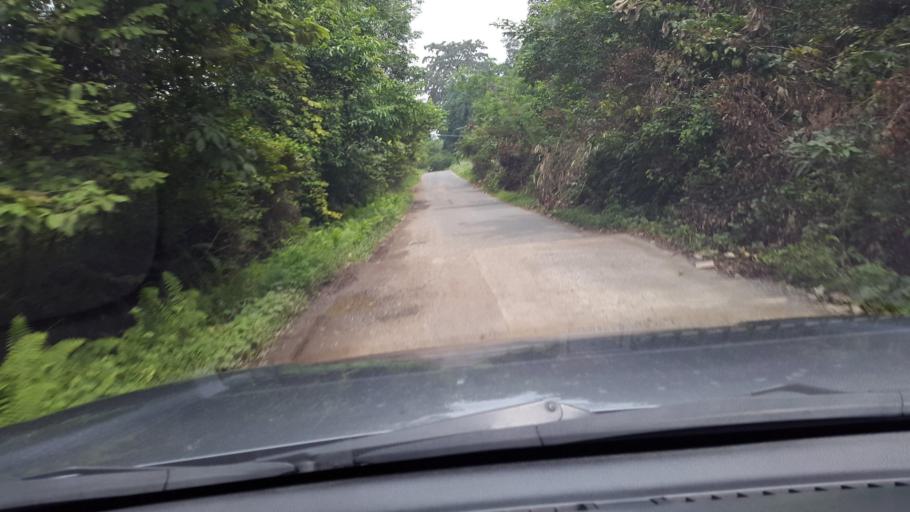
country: ID
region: South Sumatra
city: Sekayu
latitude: -3.0984
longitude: 103.8203
